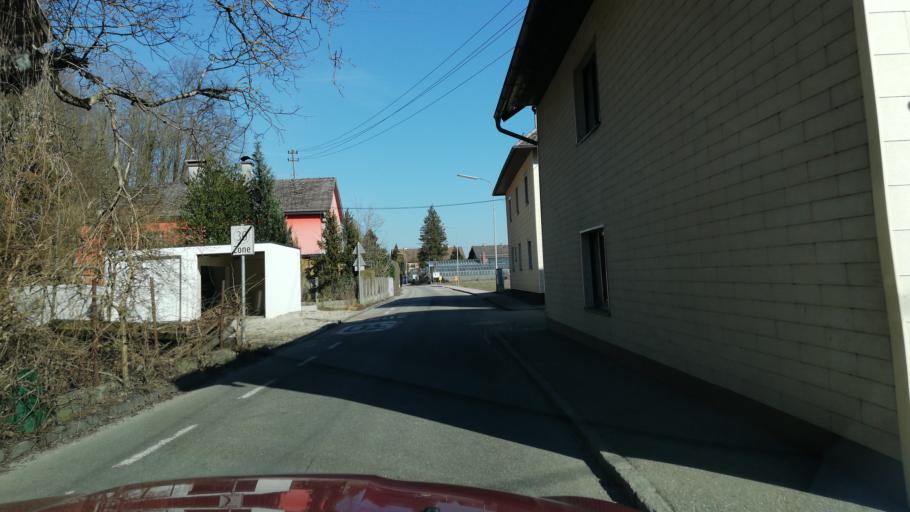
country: AT
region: Upper Austria
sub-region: Politischer Bezirk Vocklabruck
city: Redlham
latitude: 48.0152
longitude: 13.7305
